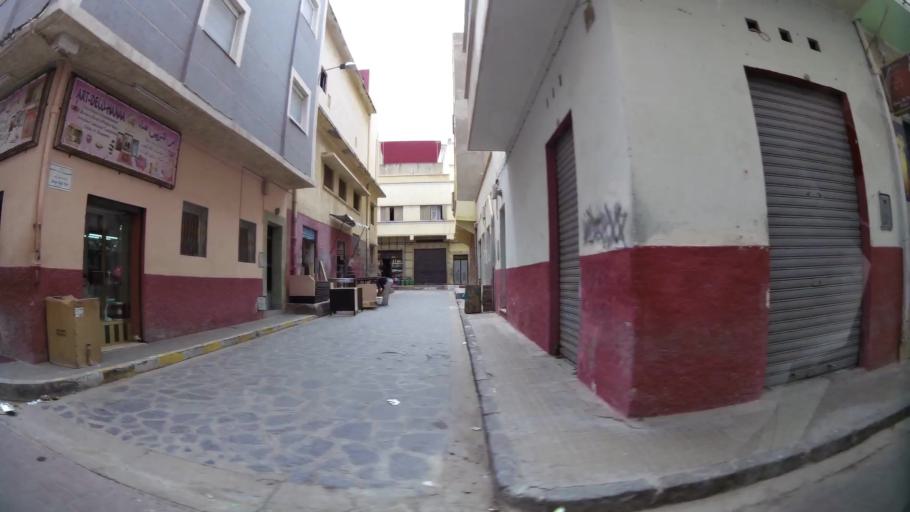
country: MA
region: Oriental
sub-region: Nador
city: Nador
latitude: 35.1739
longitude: -2.9269
